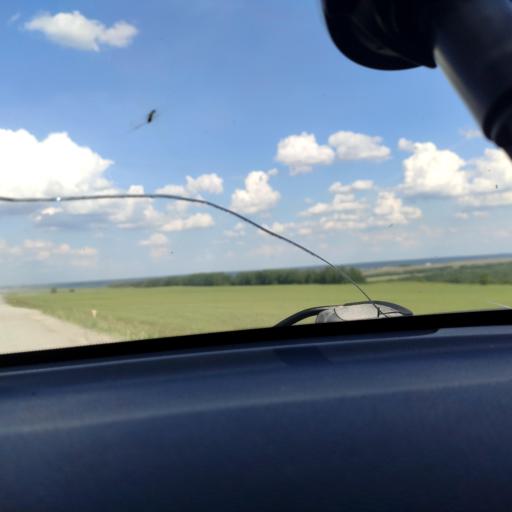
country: RU
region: Tatarstan
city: Verkhniy Uslon
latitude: 55.6423
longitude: 48.9012
